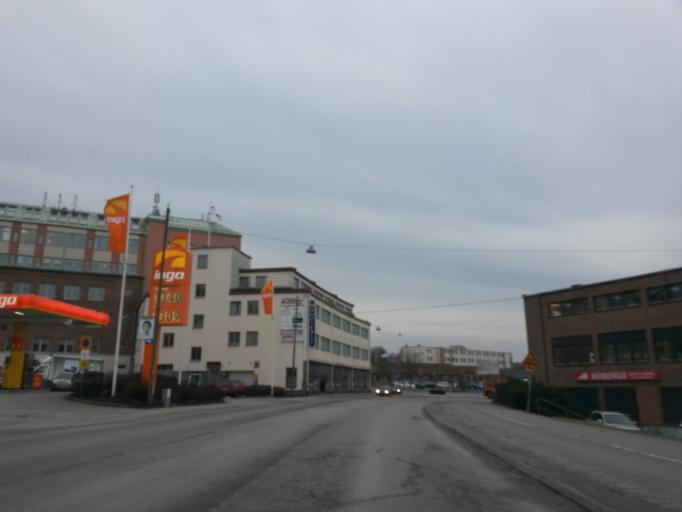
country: SE
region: Vaestra Goetaland
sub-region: Boras Kommun
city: Boras
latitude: 57.7307
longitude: 12.9394
